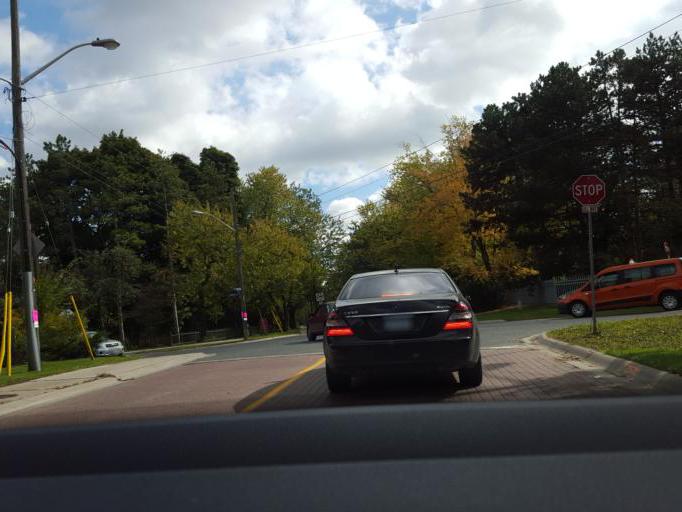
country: CA
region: Ontario
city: Willowdale
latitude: 43.7337
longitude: -79.3653
